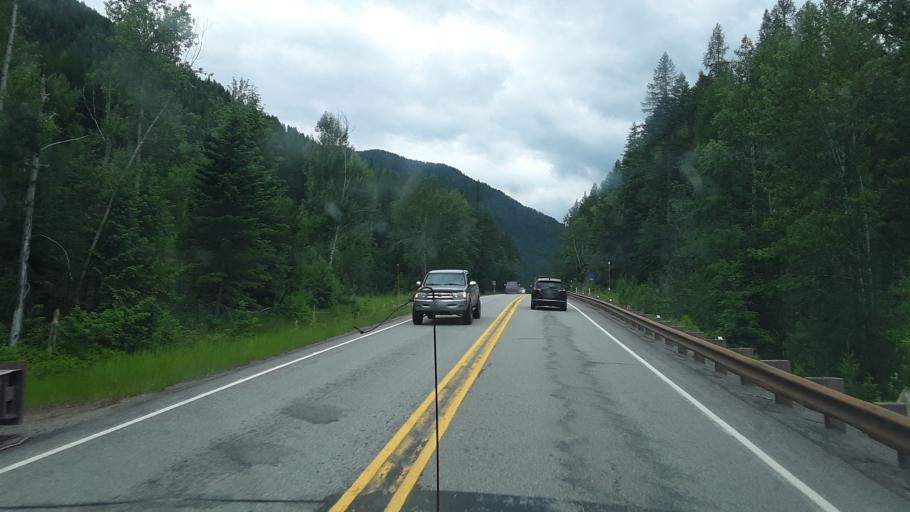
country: US
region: Montana
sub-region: Flathead County
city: Columbia Falls
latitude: 48.4943
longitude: -113.8881
